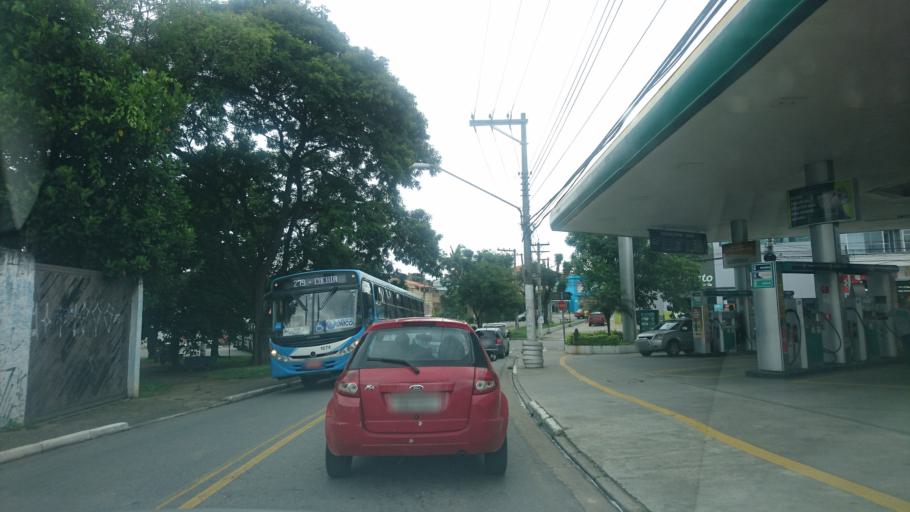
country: BR
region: Sao Paulo
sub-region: Guarulhos
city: Guarulhos
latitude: -23.4544
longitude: -46.5280
